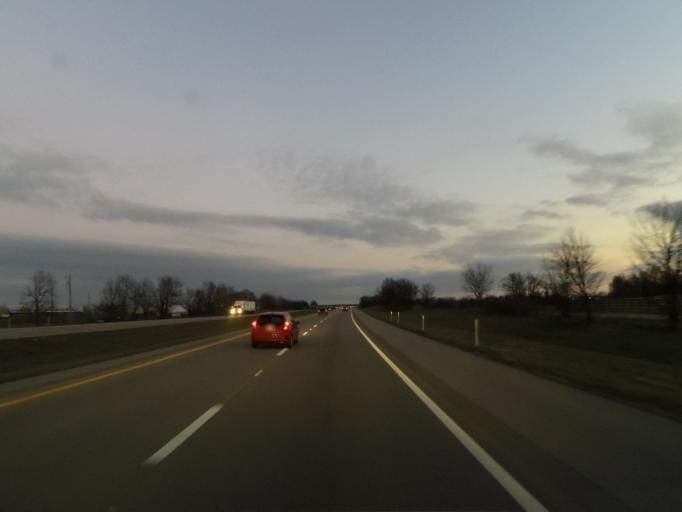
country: US
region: Kentucky
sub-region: Scott County
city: Georgetown
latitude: 38.1420
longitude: -84.5733
